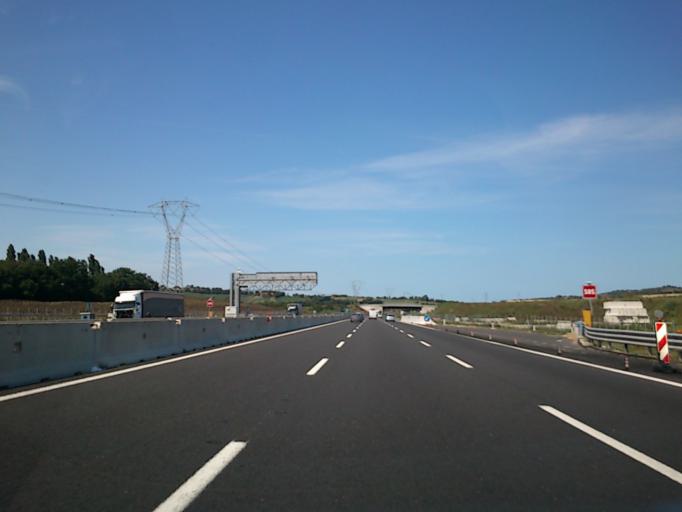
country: IT
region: The Marches
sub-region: Provincia di Pesaro e Urbino
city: Borgo Santa Maria
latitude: 43.9051
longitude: 12.8266
